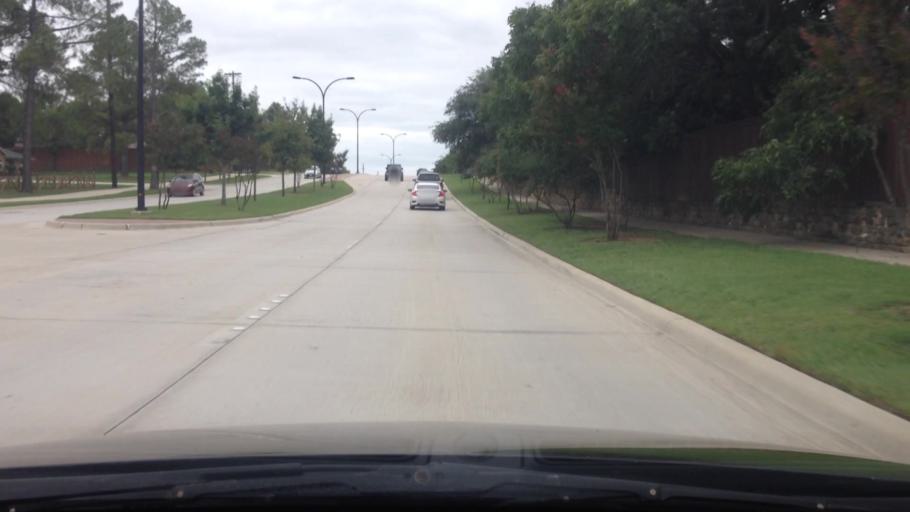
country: US
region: Texas
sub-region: Tarrant County
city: Keller
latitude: 32.9179
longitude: -97.2322
